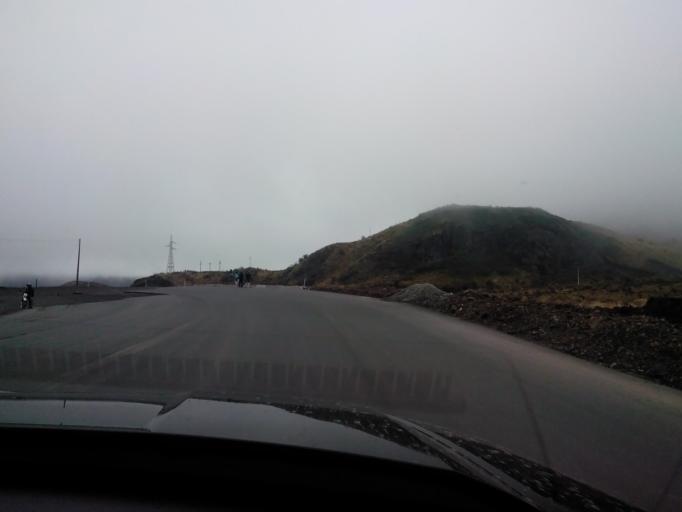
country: EC
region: Pichincha
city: Sangolqui
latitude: -0.3325
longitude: -78.2019
